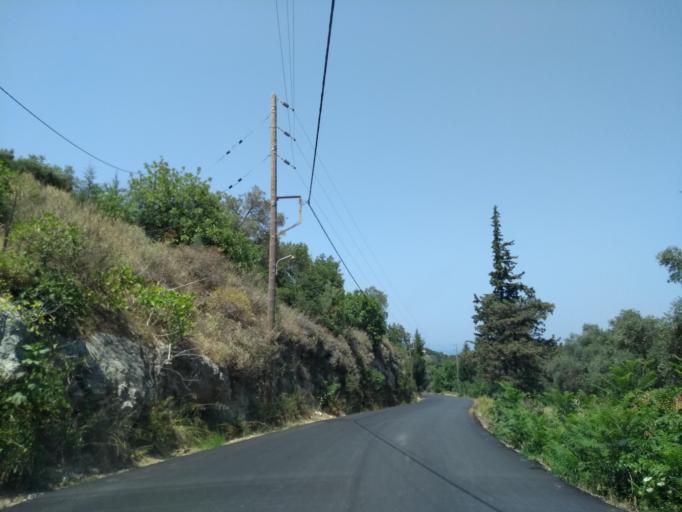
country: GR
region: Crete
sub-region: Nomos Chanias
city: Georgioupolis
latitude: 35.3172
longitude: 24.2986
